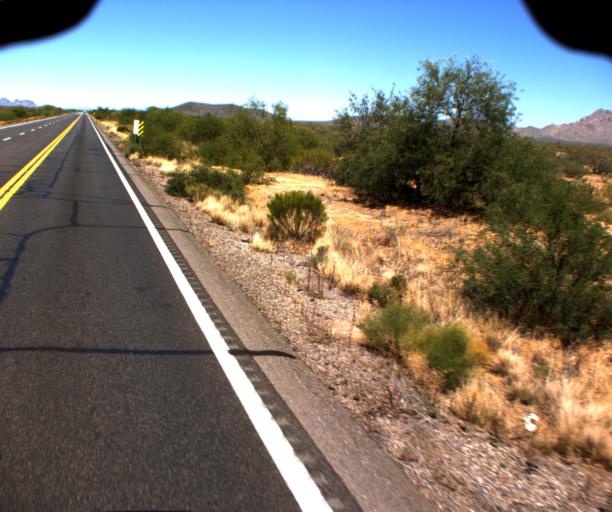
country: US
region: Arizona
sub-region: Yavapai County
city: Congress
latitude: 34.1464
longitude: -112.9836
